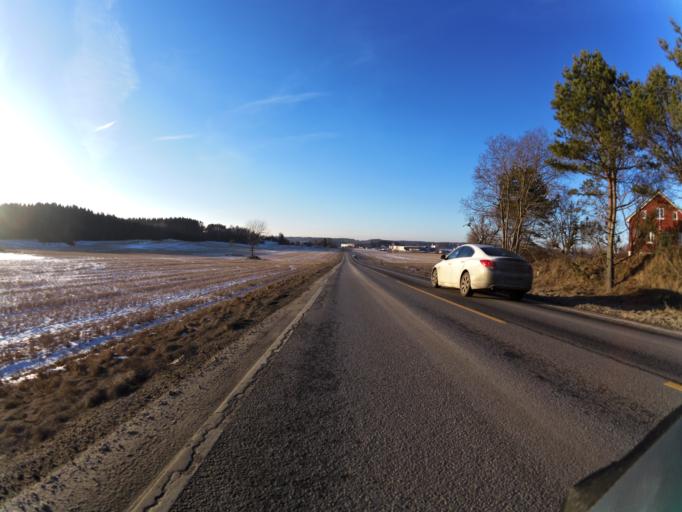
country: NO
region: Ostfold
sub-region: Fredrikstad
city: Lervik
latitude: 59.2616
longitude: 10.8164
